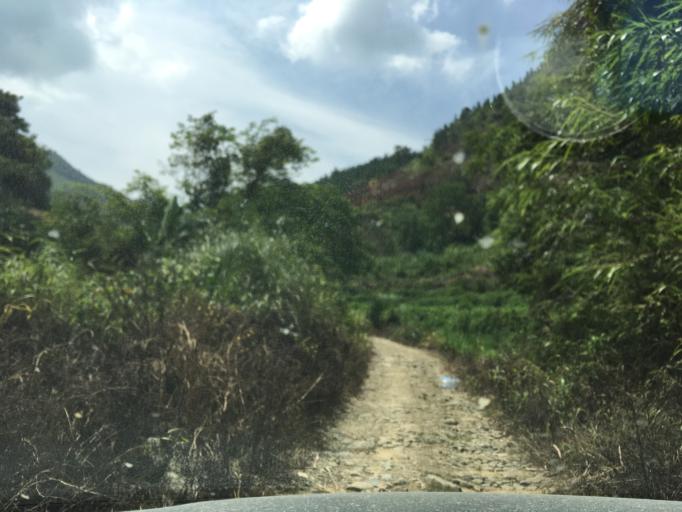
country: CN
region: Guangxi Zhuangzu Zizhiqu
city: Xinzhou
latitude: 24.9535
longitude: 105.7917
